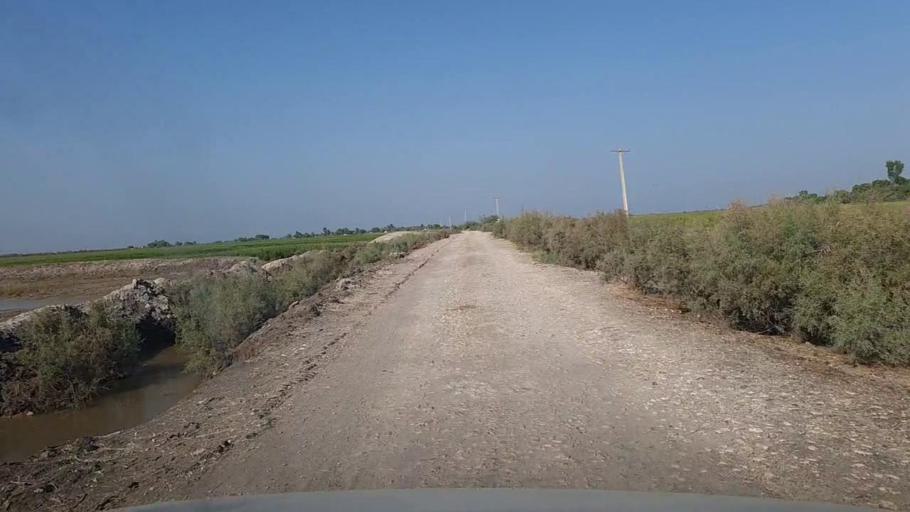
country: PK
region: Sindh
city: Kandhkot
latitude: 28.2723
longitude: 69.3126
